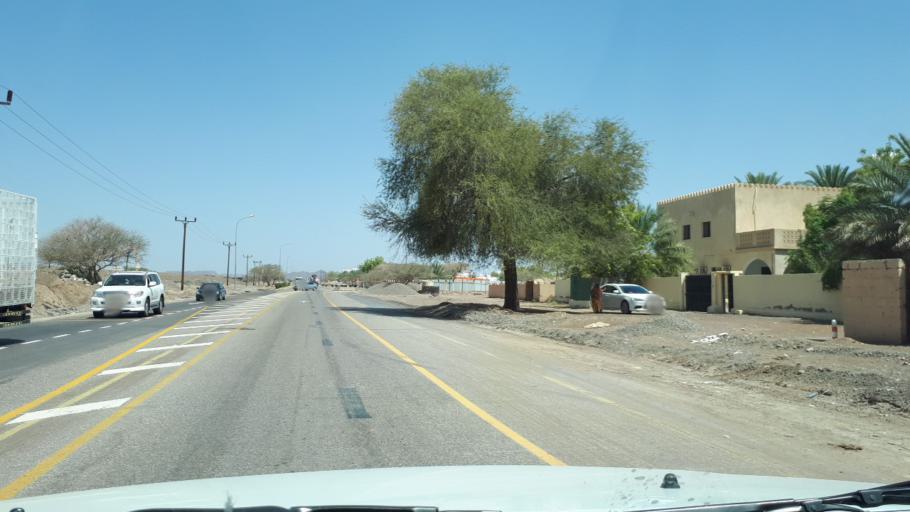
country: OM
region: Ash Sharqiyah
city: Al Qabil
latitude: 22.6083
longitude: 58.6661
